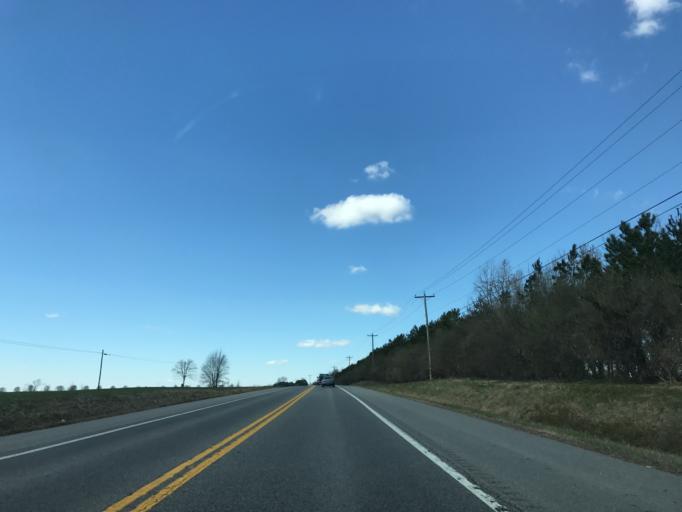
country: US
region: Maryland
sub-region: Queen Anne's County
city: Kingstown
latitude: 39.1825
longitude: -76.0068
